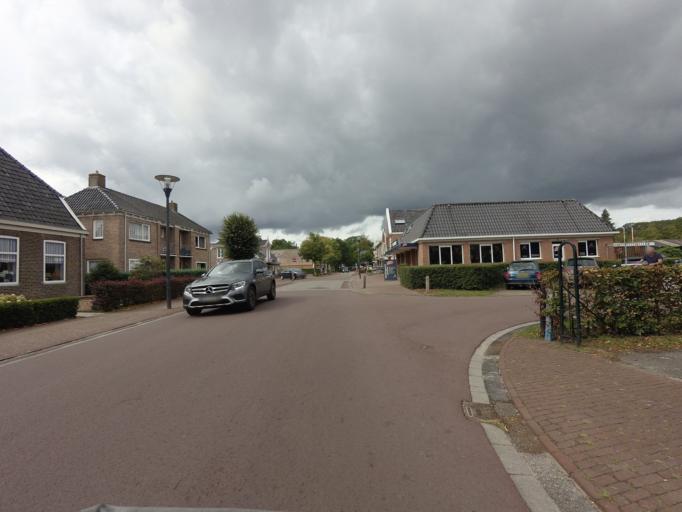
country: NL
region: Drenthe
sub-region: Gemeente Tynaarlo
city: Vries
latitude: 53.0670
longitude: 6.4645
